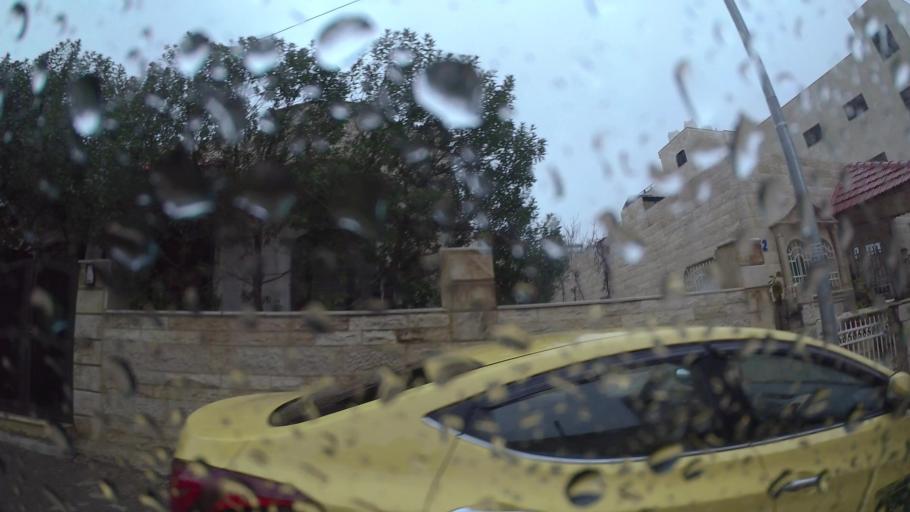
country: JO
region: Amman
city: Al Jubayhah
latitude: 32.0465
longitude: 35.8781
